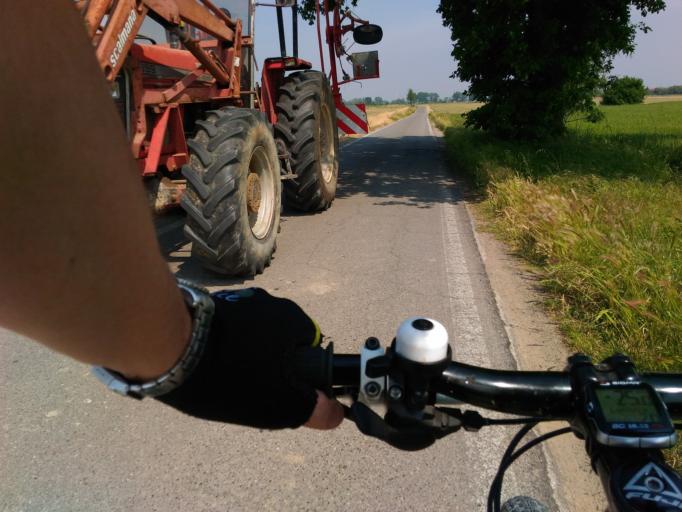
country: IT
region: Lombardy
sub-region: Provincia di Lodi
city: Villanova del Sillaro
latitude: 45.2456
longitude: 9.4720
